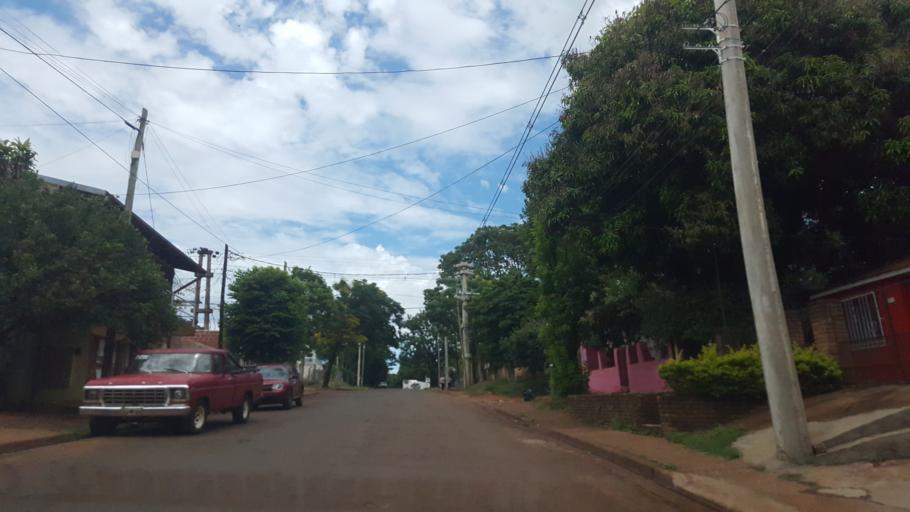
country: AR
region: Misiones
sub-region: Departamento de Capital
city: Posadas
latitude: -27.4283
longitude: -55.8892
